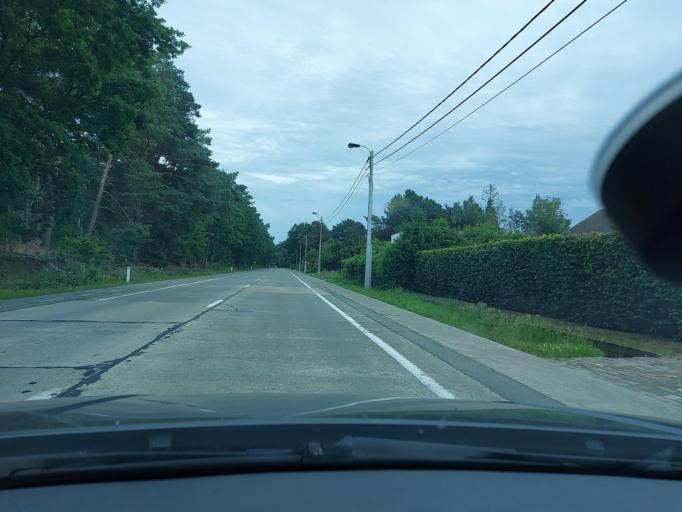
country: BE
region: Flanders
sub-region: Provincie Antwerpen
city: Balen
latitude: 51.1914
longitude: 5.1923
